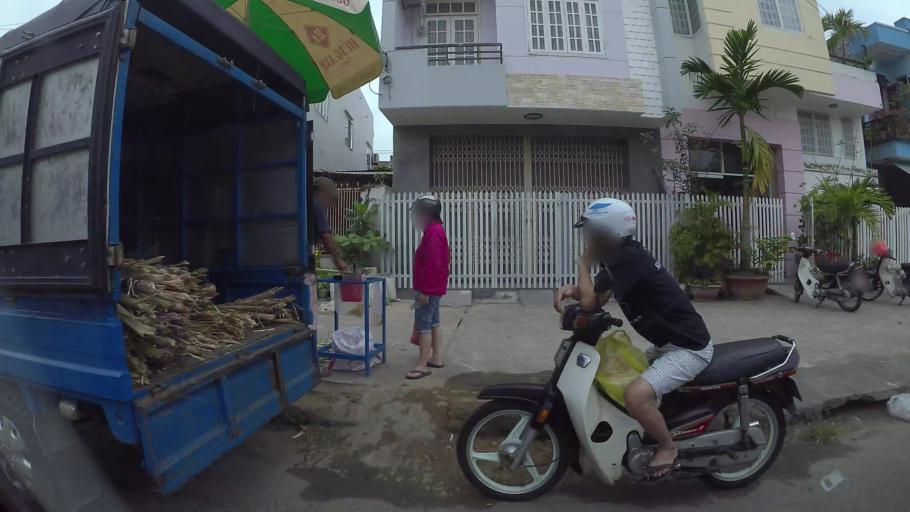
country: VN
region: Da Nang
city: Thanh Khe
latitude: 16.0696
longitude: 108.1850
